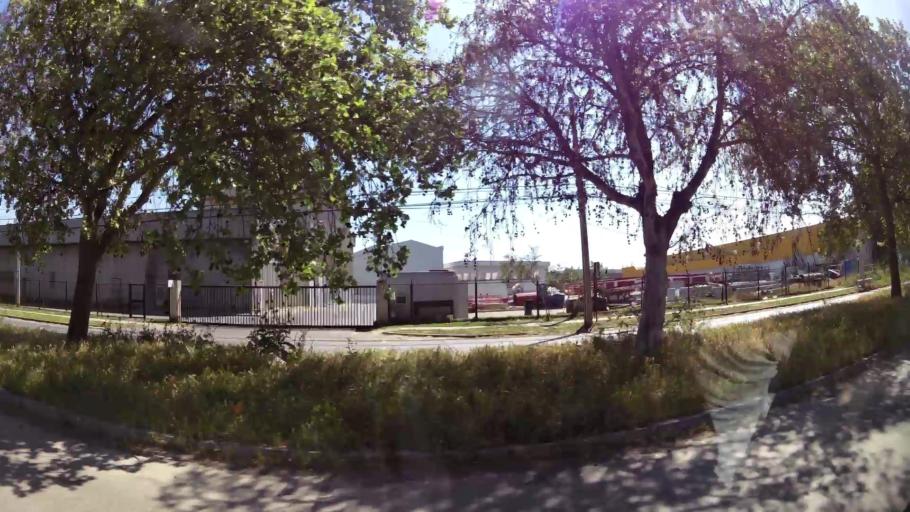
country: CL
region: Santiago Metropolitan
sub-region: Provincia de Santiago
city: Lo Prado
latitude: -33.3832
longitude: -70.7472
